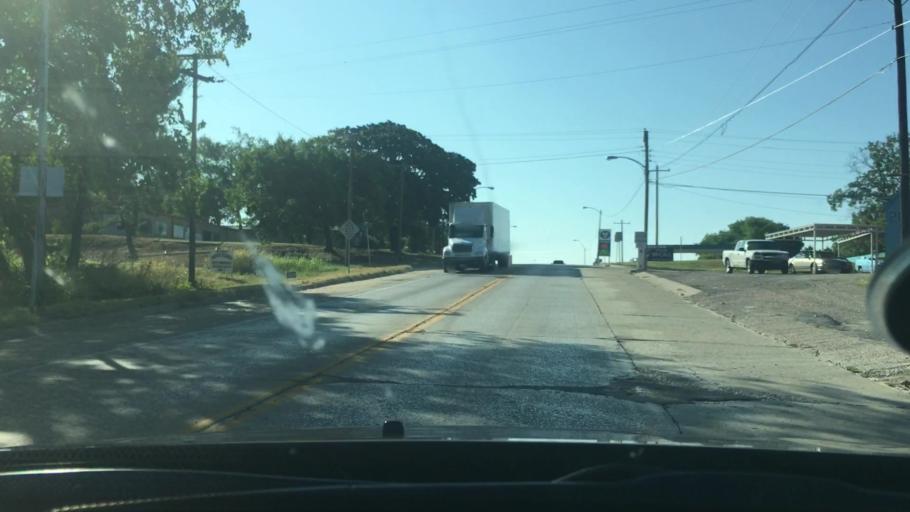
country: US
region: Oklahoma
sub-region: Johnston County
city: Tishomingo
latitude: 34.2387
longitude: -96.6844
